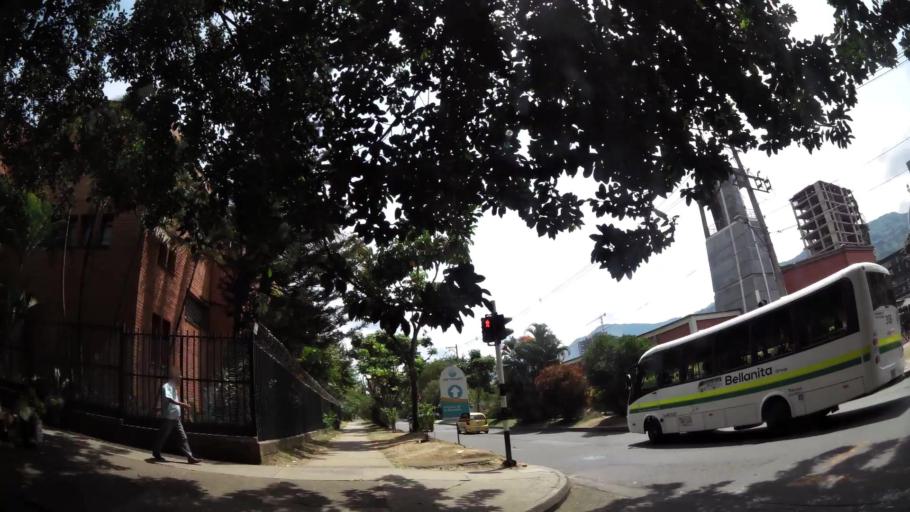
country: CO
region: Antioquia
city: Bello
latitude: 6.3411
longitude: -75.5457
